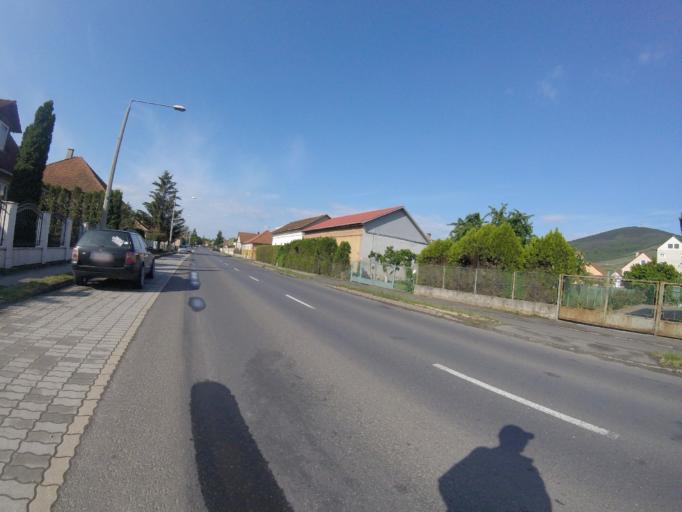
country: HU
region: Borsod-Abauj-Zemplen
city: Tokaj
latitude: 48.1103
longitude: 21.4100
